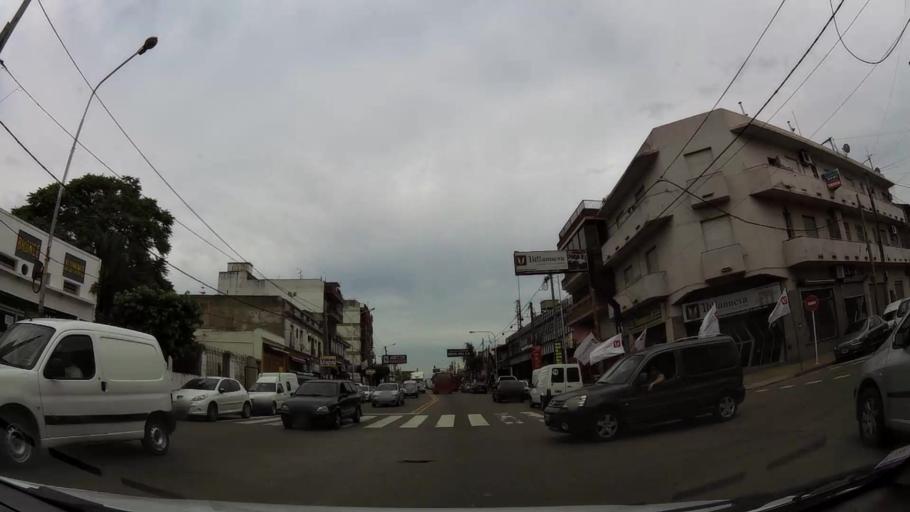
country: AR
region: Buenos Aires F.D.
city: Villa Lugano
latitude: -34.6761
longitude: -58.5054
